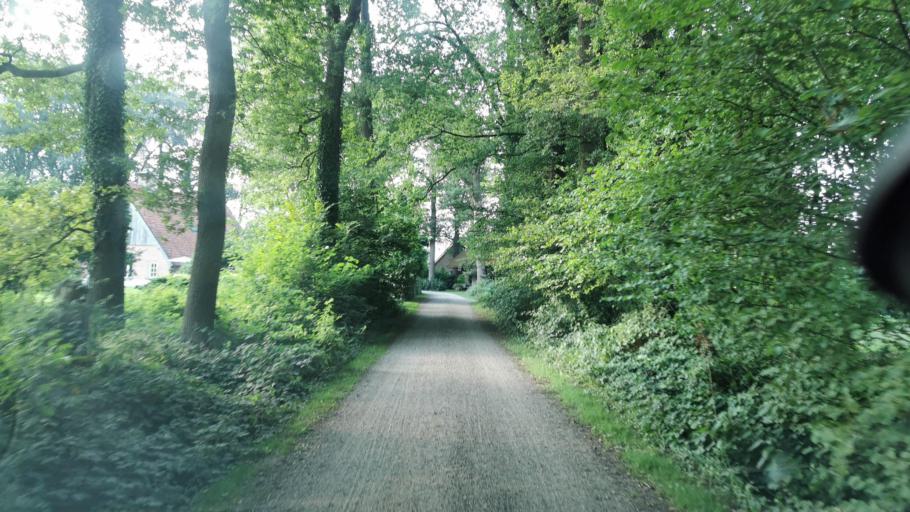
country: NL
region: Overijssel
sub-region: Gemeente Oldenzaal
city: Oldenzaal
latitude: 52.3020
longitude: 6.9555
